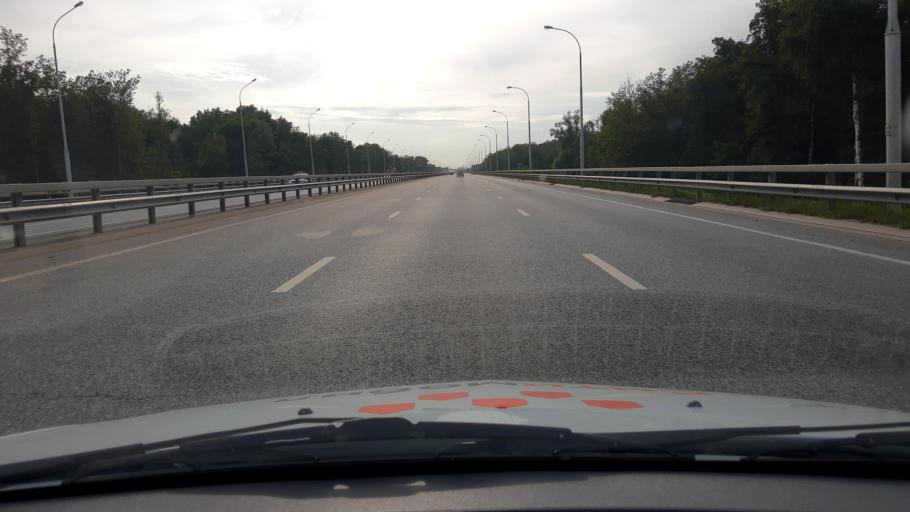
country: RU
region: Bashkortostan
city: Ufa
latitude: 54.6491
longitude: 56.0441
